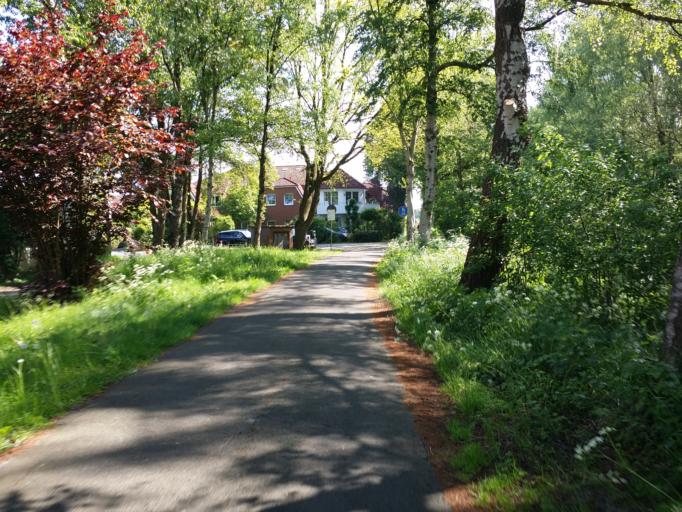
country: DE
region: Lower Saxony
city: Lilienthal
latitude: 53.1510
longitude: 8.9298
